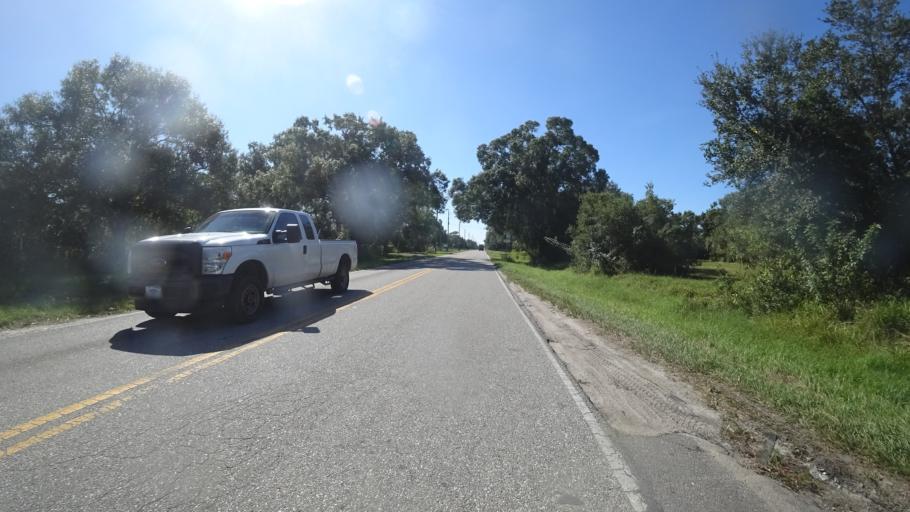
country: US
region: Florida
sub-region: Sarasota County
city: Lake Sarasota
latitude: 27.3870
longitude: -82.2682
